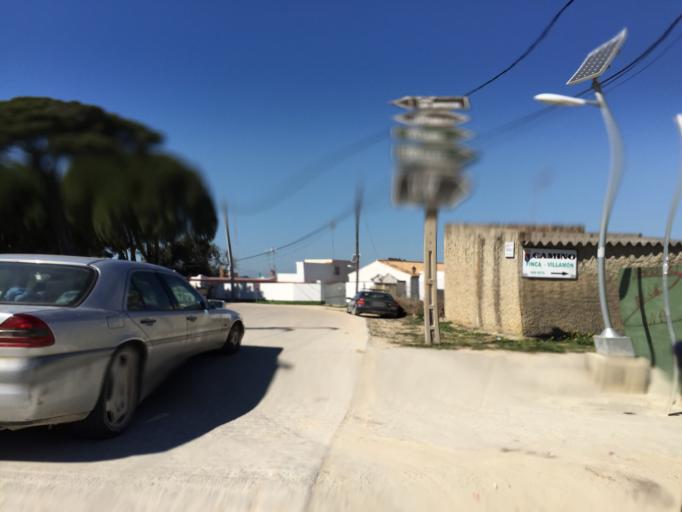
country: ES
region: Andalusia
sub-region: Provincia de Cadiz
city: Vejer de la Frontera
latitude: 36.2057
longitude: -5.9806
